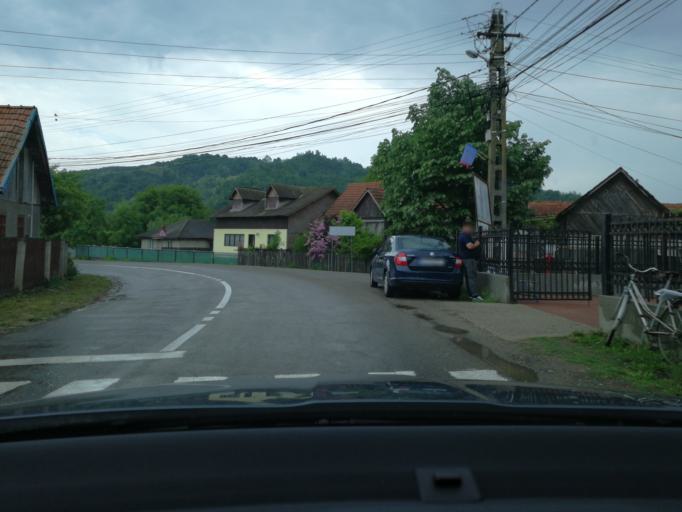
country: RO
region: Prahova
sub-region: Comuna Alunis
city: Ostrovu
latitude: 45.2010
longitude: 25.9005
